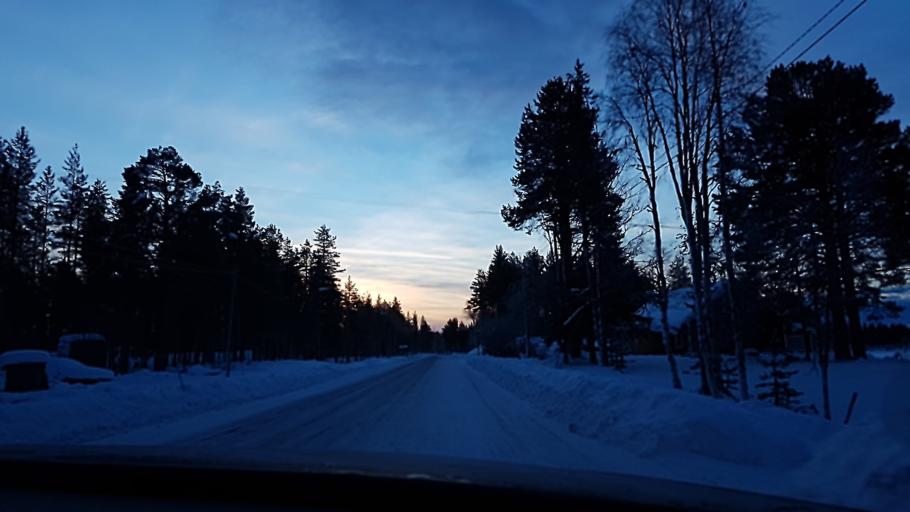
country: SE
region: Norrbotten
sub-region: Jokkmokks Kommun
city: Jokkmokk
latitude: 66.1400
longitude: 20.0006
